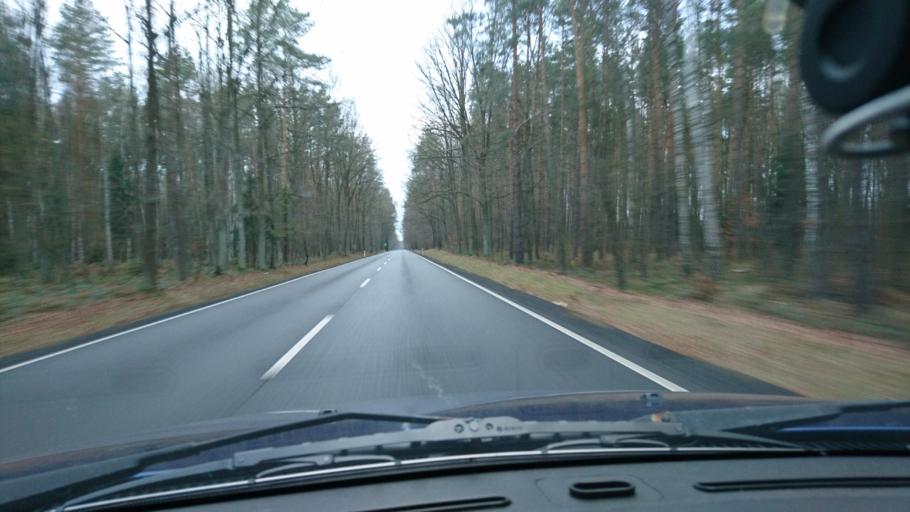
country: PL
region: Opole Voivodeship
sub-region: Powiat oleski
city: Olesno
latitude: 50.9245
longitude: 18.3373
